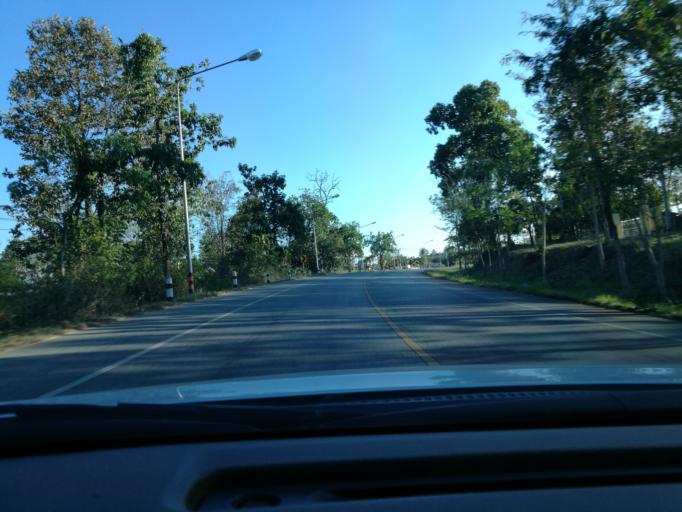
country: TH
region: Phitsanulok
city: Nakhon Thai
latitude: 17.0337
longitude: 100.8193
